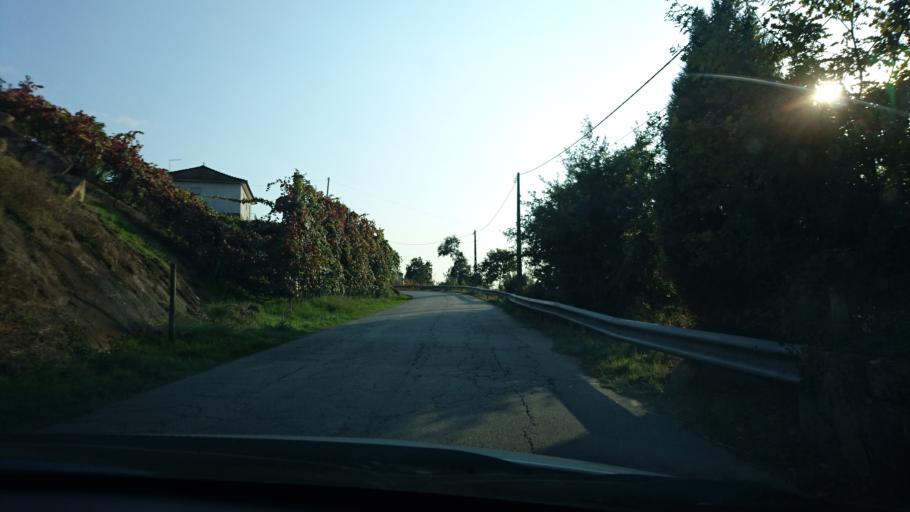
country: PT
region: Vila Real
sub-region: Mondim de Basto
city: Mondim de Basto
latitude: 41.4414
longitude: -7.9265
